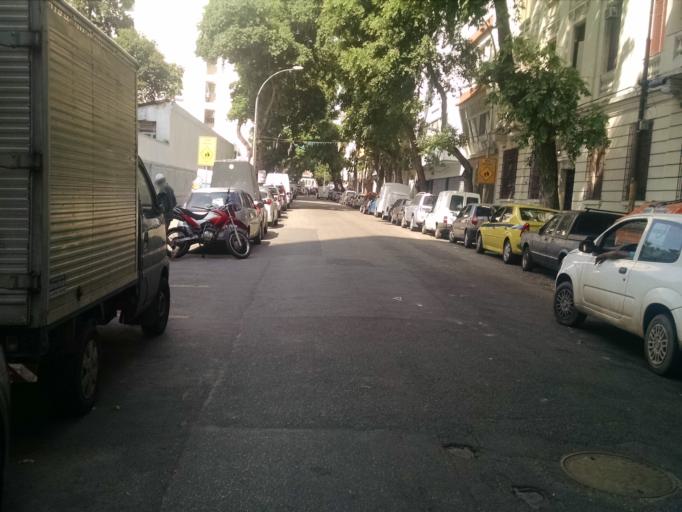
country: BR
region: Rio de Janeiro
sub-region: Rio De Janeiro
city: Rio de Janeiro
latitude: -22.9125
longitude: -43.1866
